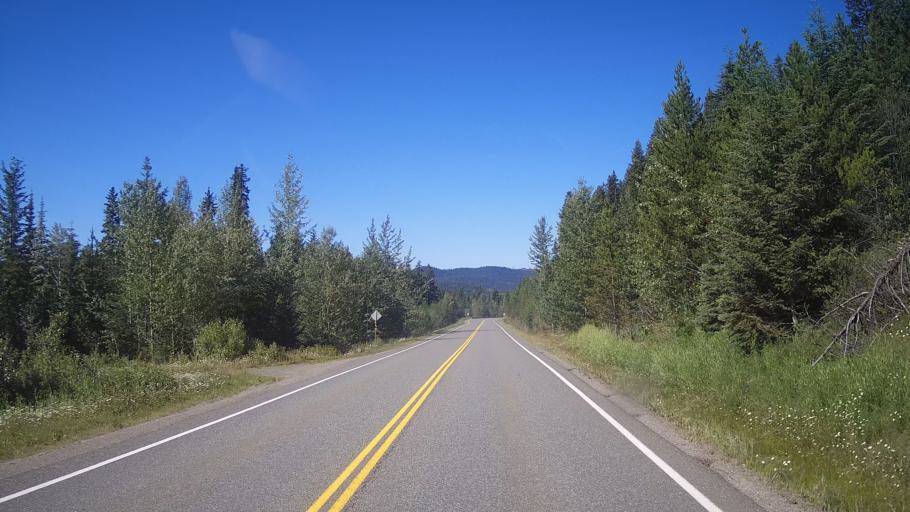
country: CA
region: British Columbia
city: Kamloops
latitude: 51.4786
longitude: -120.4704
